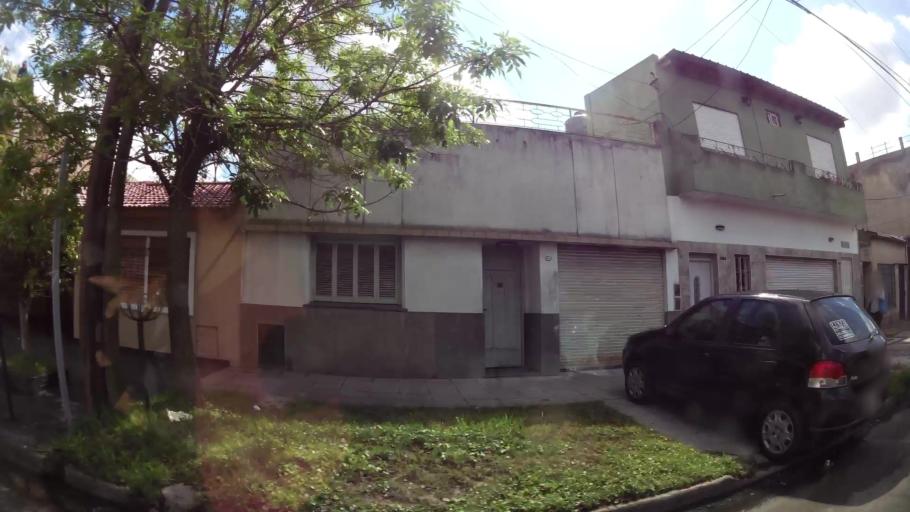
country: AR
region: Buenos Aires
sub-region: Partido de Lanus
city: Lanus
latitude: -34.6896
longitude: -58.4124
